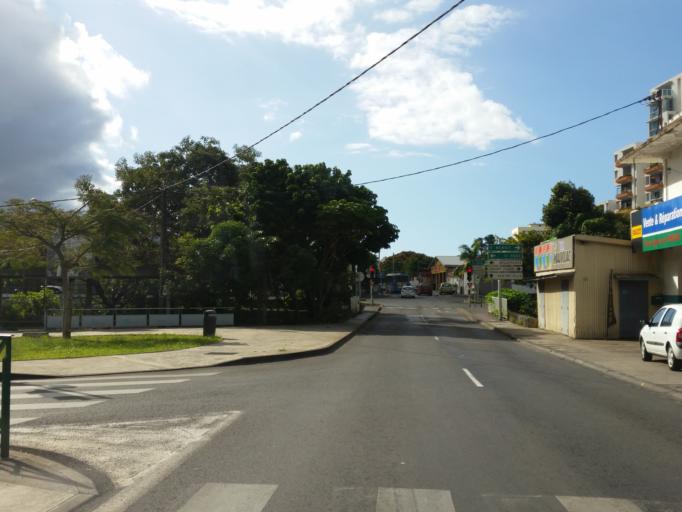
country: RE
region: Reunion
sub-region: Reunion
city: Saint-Denis
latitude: -20.8914
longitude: 55.4549
